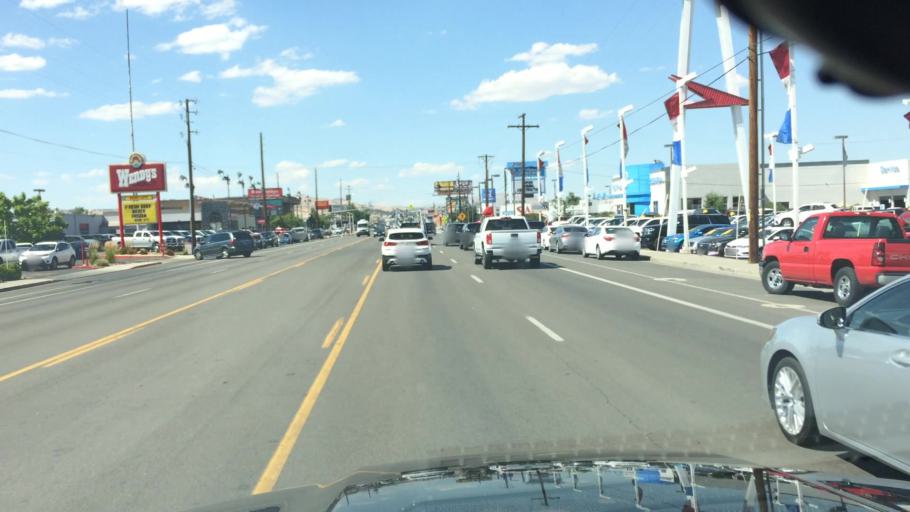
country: US
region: Nevada
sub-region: Washoe County
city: Reno
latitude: 39.5181
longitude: -119.7892
